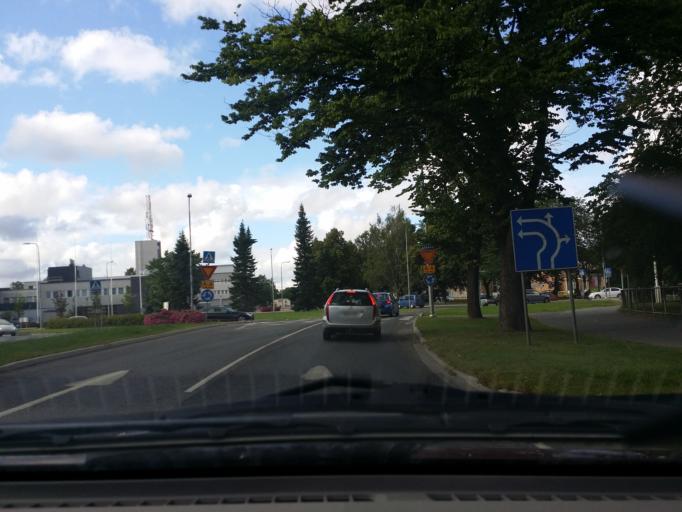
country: FI
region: Satakunta
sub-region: Pori
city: Pori
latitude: 61.4803
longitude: 21.7862
